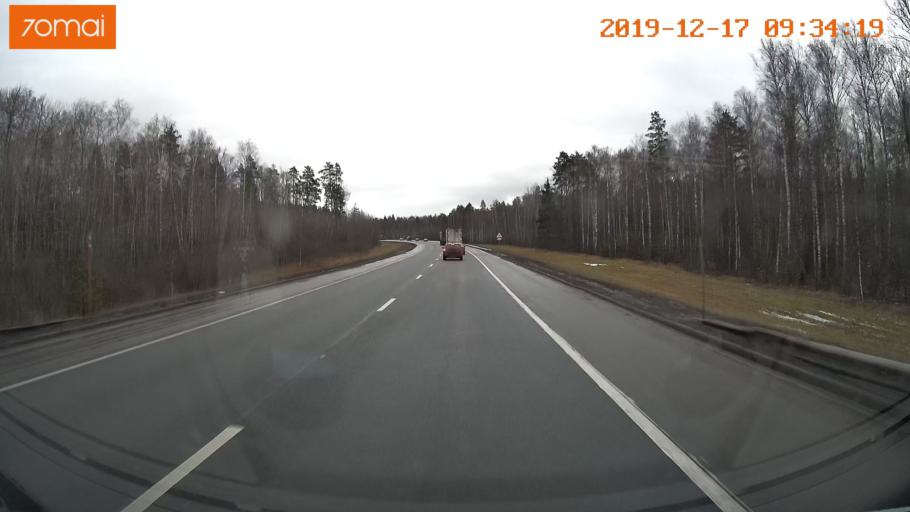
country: RU
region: Vladimir
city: Raduzhnyy
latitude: 56.0731
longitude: 40.2204
